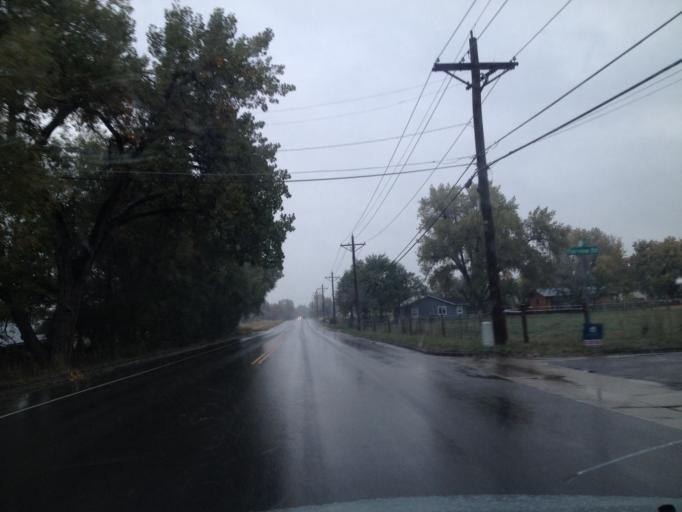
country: US
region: Colorado
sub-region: Boulder County
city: Superior
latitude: 39.9929
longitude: -105.1752
